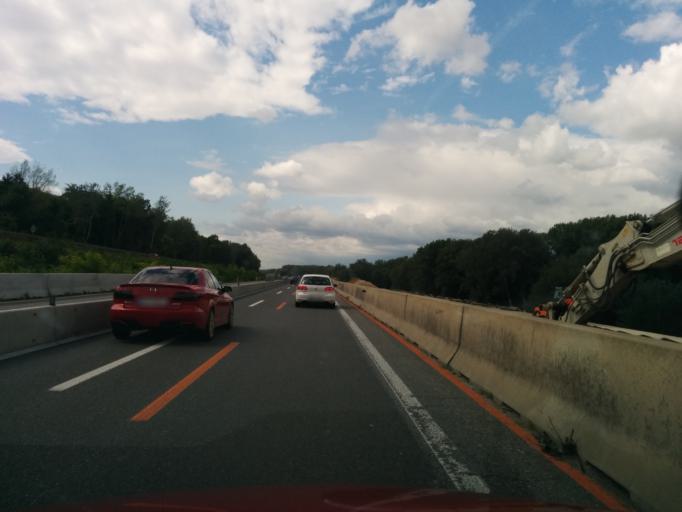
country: AT
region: Lower Austria
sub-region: Politischer Bezirk Wien-Umgebung
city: Fischamend Dorf
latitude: 48.1270
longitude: 16.5883
